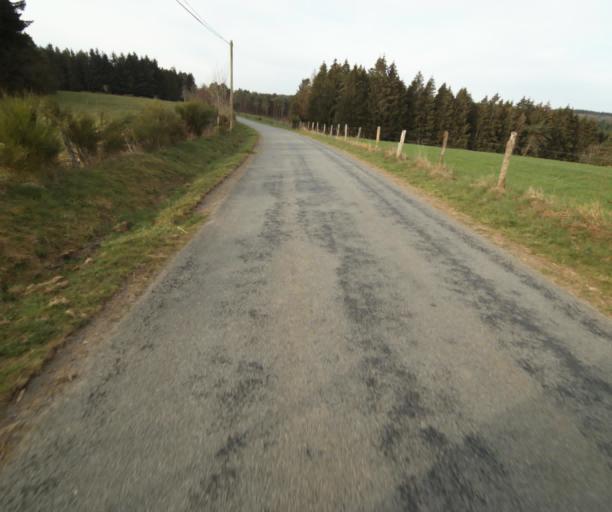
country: FR
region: Limousin
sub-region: Departement de la Correze
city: Treignac
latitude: 45.4651
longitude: 1.8175
